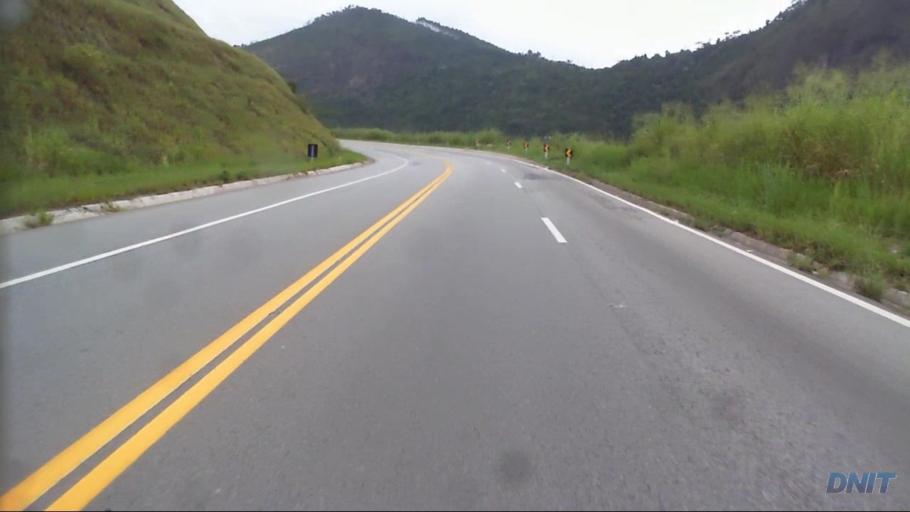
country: BR
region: Minas Gerais
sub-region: Nova Era
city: Nova Era
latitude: -19.6498
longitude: -42.9387
